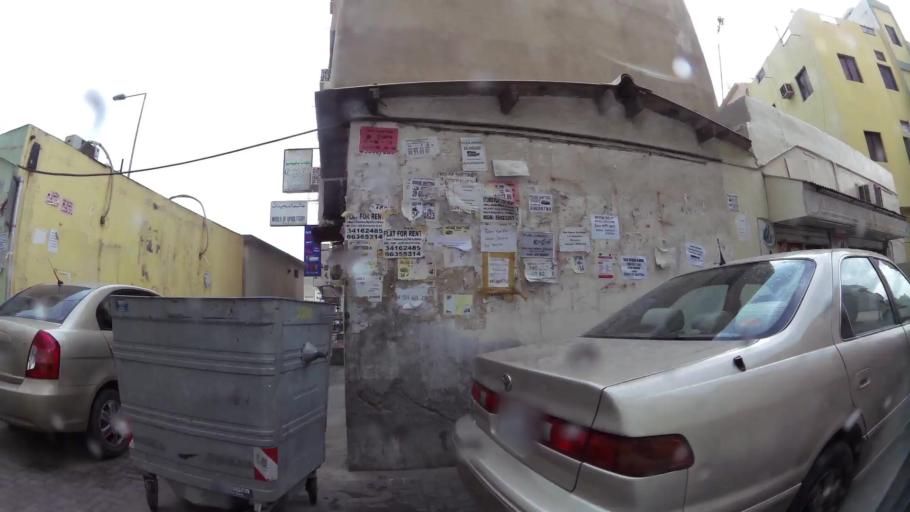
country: BH
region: Manama
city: Manama
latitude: 26.2269
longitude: 50.5913
